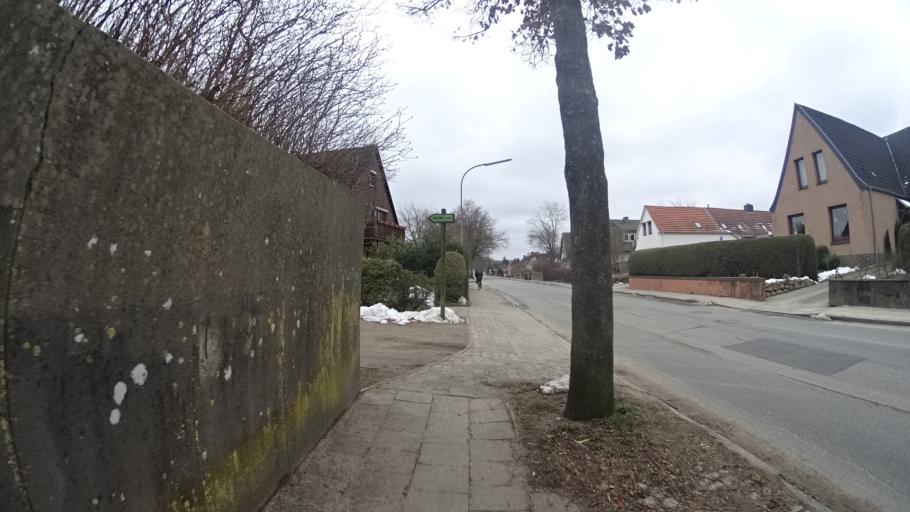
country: DE
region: Schleswig-Holstein
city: Malente
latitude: 54.1853
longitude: 10.5636
